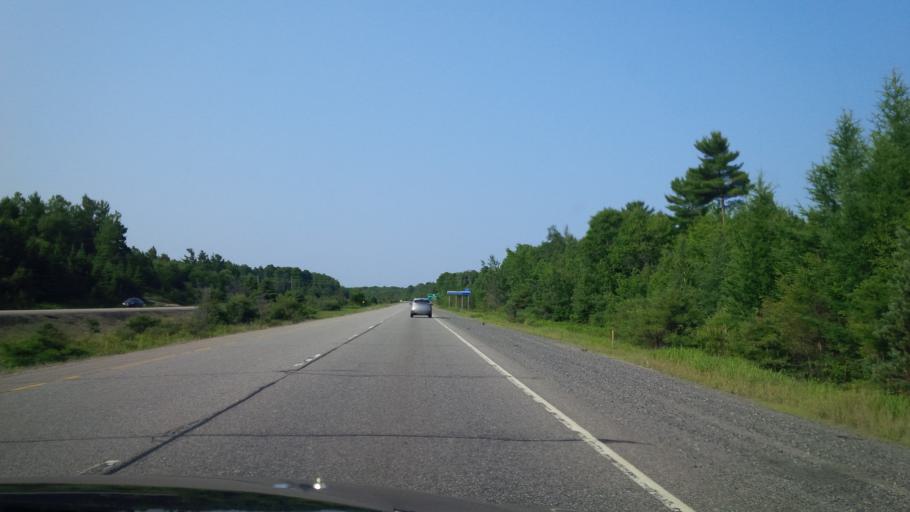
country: CA
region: Ontario
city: Huntsville
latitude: 45.2308
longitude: -79.3067
